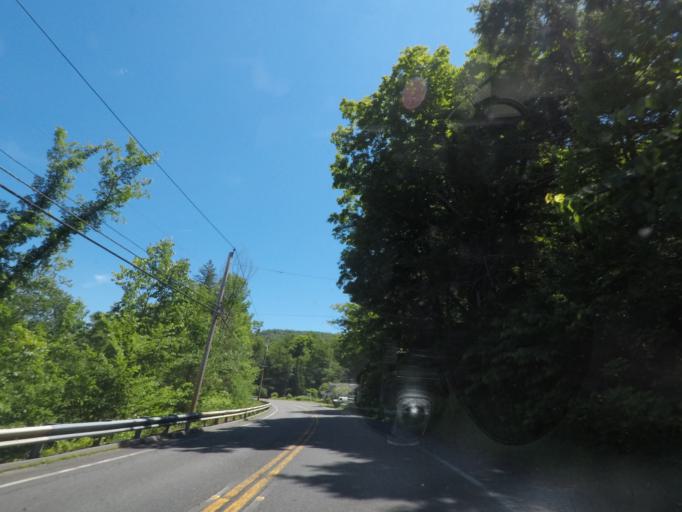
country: US
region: Massachusetts
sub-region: Berkshire County
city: Becket
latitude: 42.2587
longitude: -72.9559
